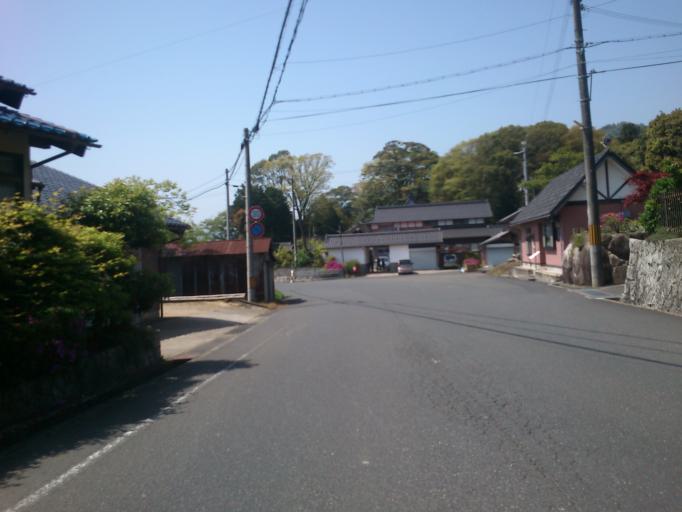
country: JP
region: Kyoto
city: Miyazu
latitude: 35.6108
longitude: 135.2218
